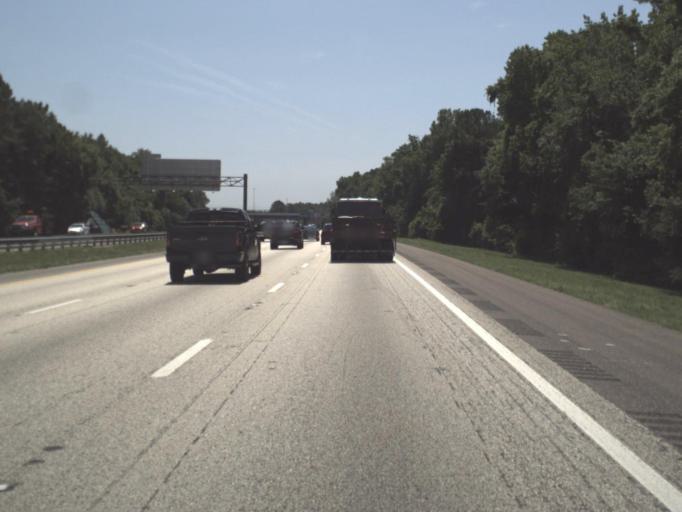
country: US
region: Florida
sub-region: Saint Johns County
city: Fruit Cove
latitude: 30.1461
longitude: -81.5444
